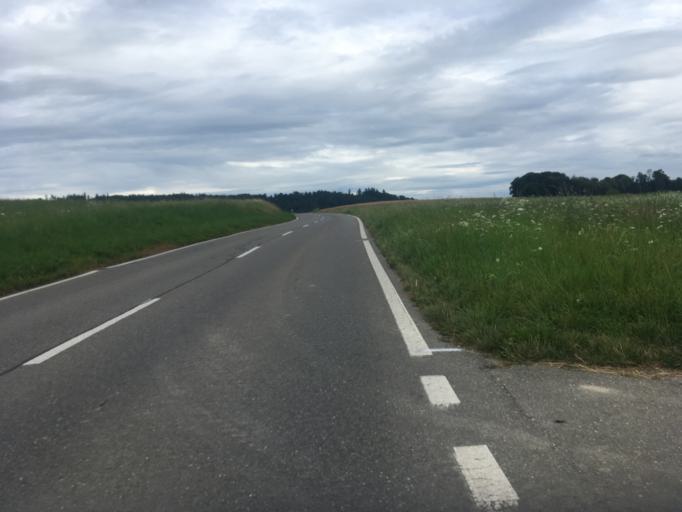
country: CH
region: Bern
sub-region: Seeland District
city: Erlach
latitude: 47.0316
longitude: 7.0944
